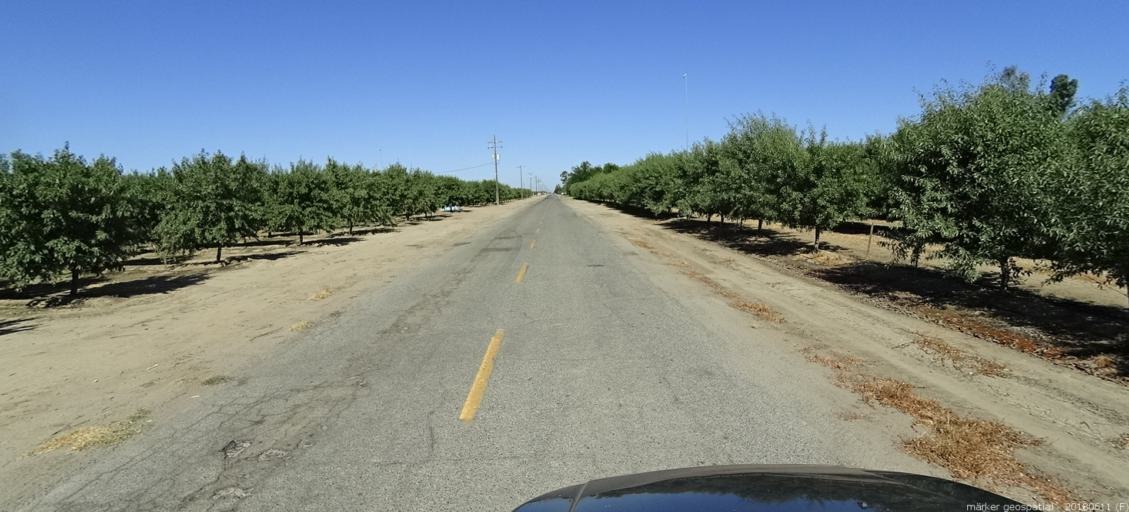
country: US
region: California
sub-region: Madera County
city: Madera
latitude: 36.9456
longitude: -120.1116
